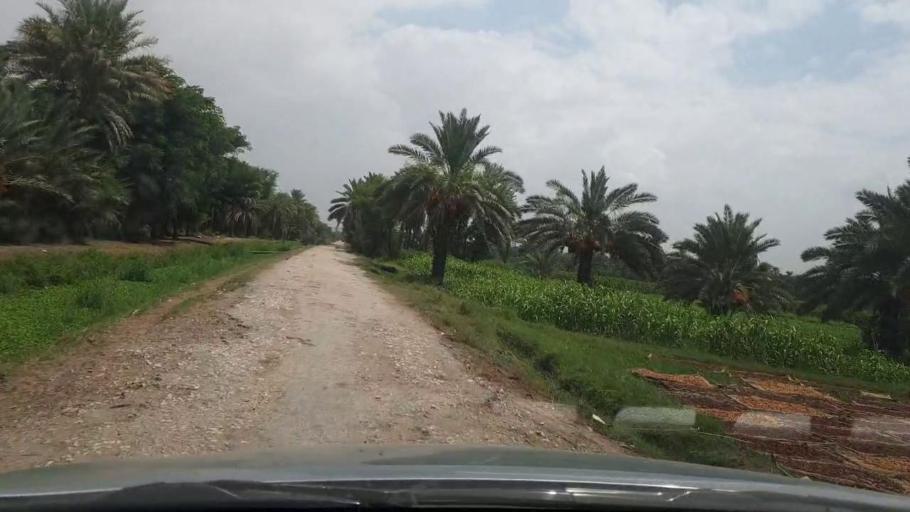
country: PK
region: Sindh
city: Kot Diji
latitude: 27.4150
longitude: 68.7592
